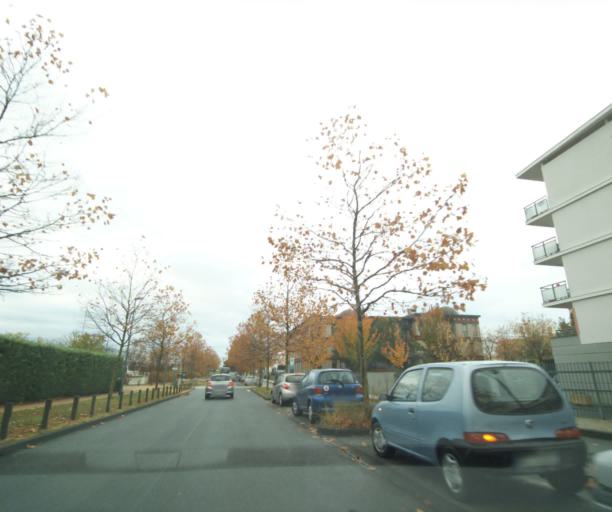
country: FR
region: Auvergne
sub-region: Departement du Puy-de-Dome
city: Cournon-d'Auvergne
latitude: 45.7419
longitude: 3.2101
